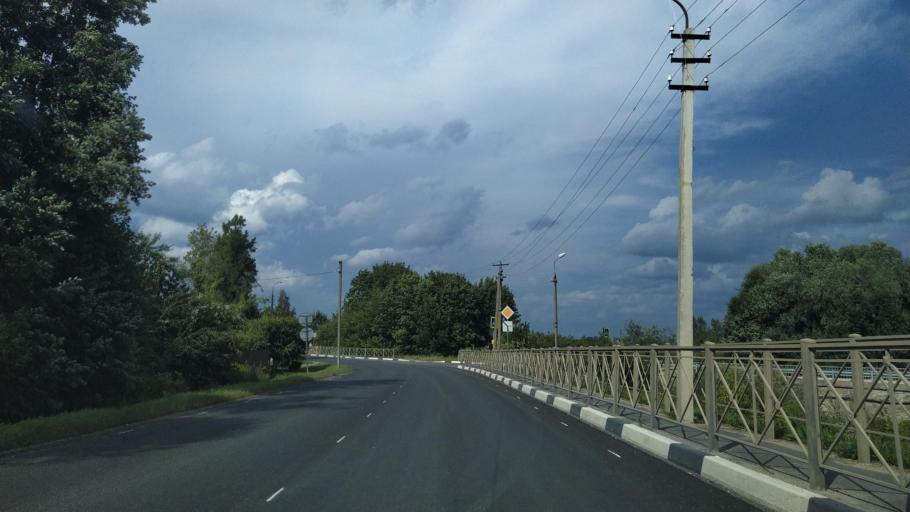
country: RU
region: Pskov
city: Porkhov
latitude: 57.7689
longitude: 29.5529
